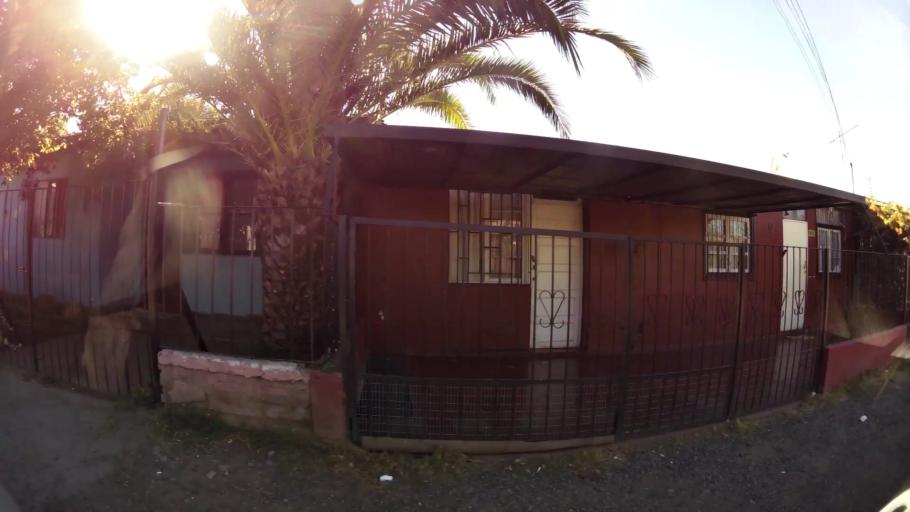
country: CL
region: O'Higgins
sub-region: Provincia de Cachapoal
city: Rancagua
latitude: -34.1844
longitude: -70.7287
